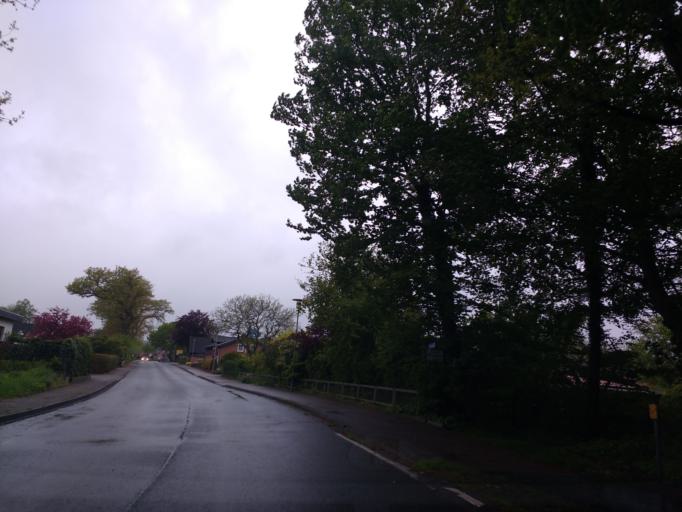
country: DE
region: Schleswig-Holstein
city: Damp
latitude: 54.5714
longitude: 9.9640
